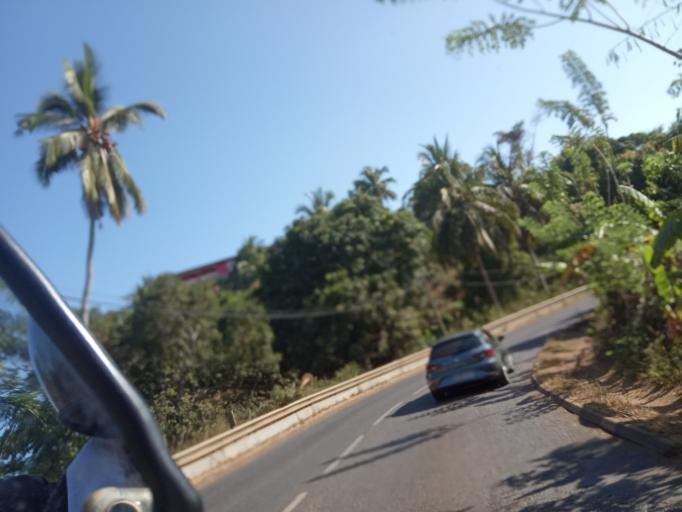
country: YT
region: Bandrele
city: Bandrele
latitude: -12.9057
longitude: 45.1922
